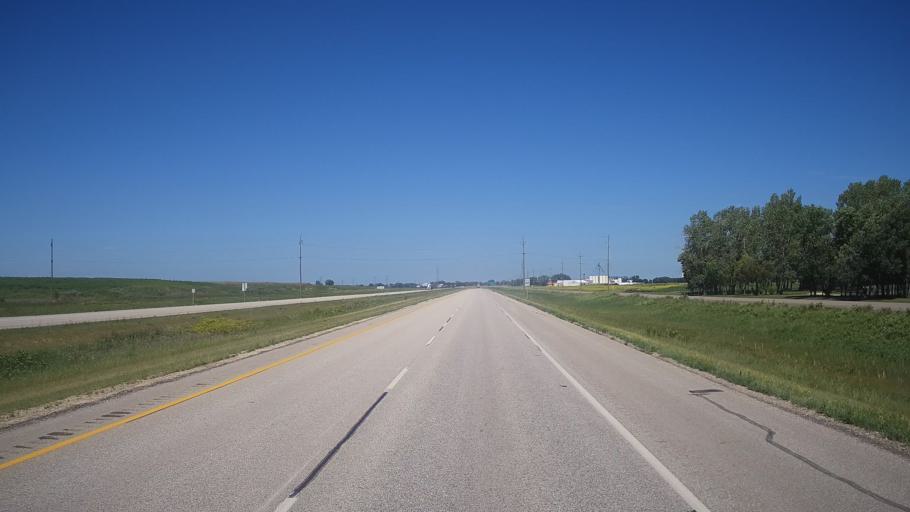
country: CA
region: Manitoba
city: Portage la Prairie
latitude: 49.9563
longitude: -98.3323
